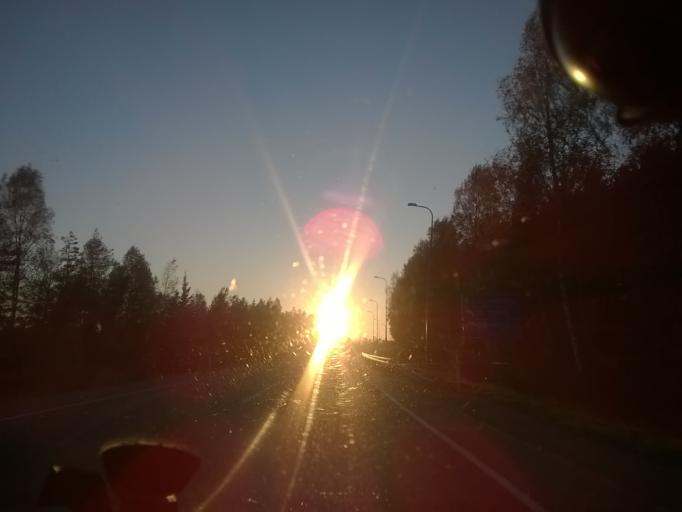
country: EE
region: Harju
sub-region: Nissi vald
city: Turba
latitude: 58.9943
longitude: 24.0640
